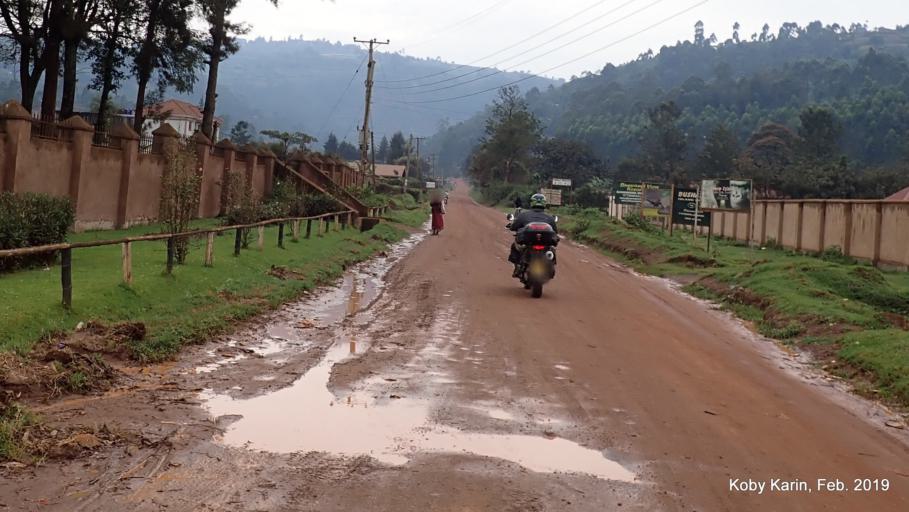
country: UG
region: Western Region
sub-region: Kabale District
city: Kabale
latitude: -1.2448
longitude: 29.9738
